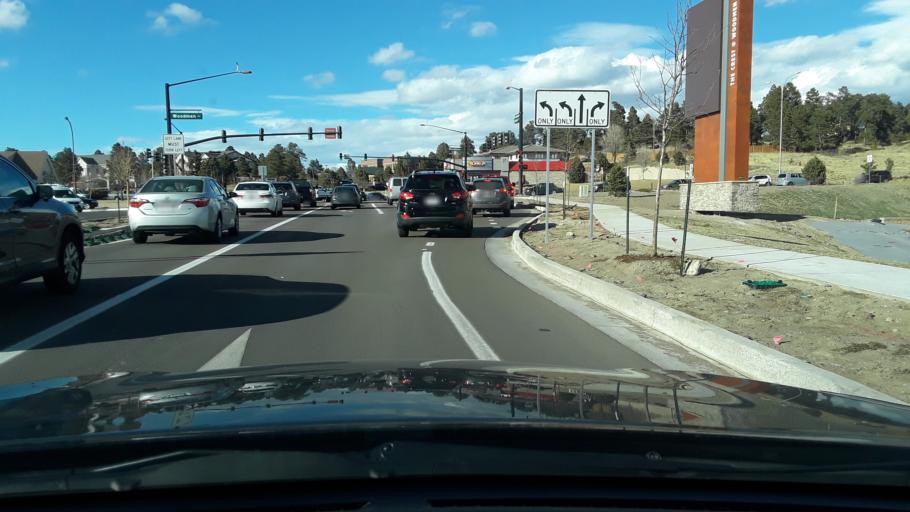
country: US
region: Colorado
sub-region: El Paso County
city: Air Force Academy
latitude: 38.9321
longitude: -104.8079
